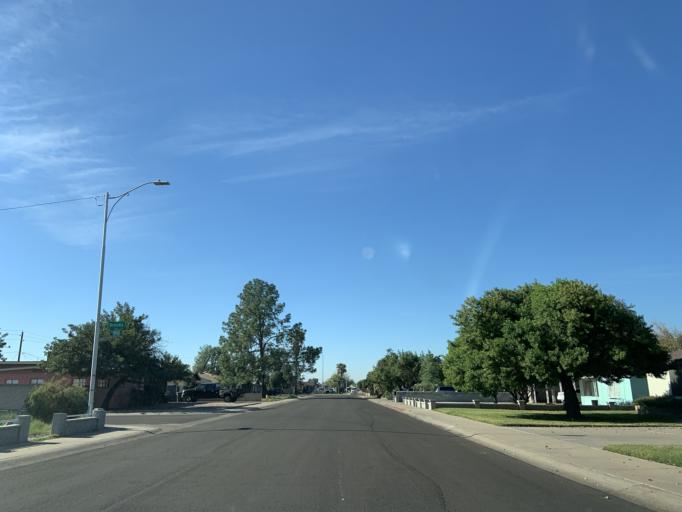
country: US
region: Arizona
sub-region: Maricopa County
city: Mesa
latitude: 33.4162
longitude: -111.8639
